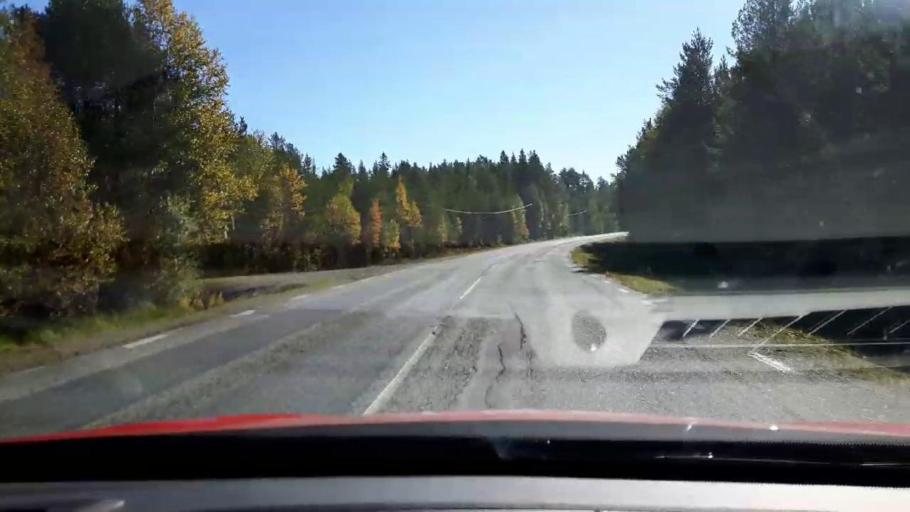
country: SE
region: Jaemtland
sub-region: Harjedalens Kommun
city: Sveg
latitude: 62.3349
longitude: 14.0530
